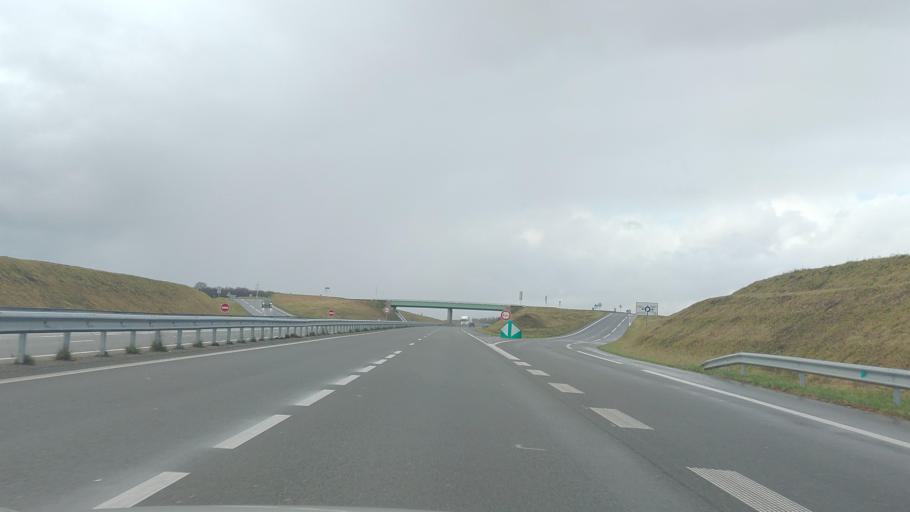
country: FR
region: Picardie
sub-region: Departement de l'Oise
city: Tille
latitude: 49.4654
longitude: 2.0802
